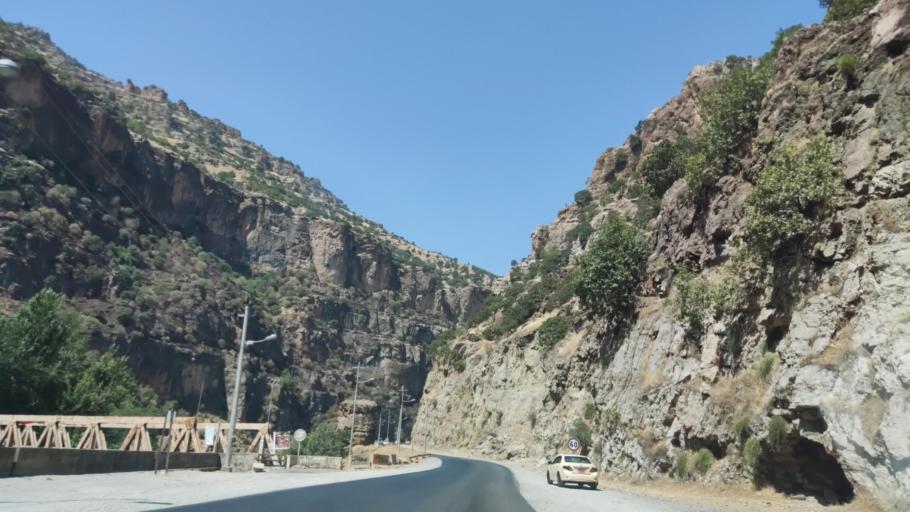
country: IQ
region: Arbil
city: Ruwandiz
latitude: 36.6268
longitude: 44.4663
